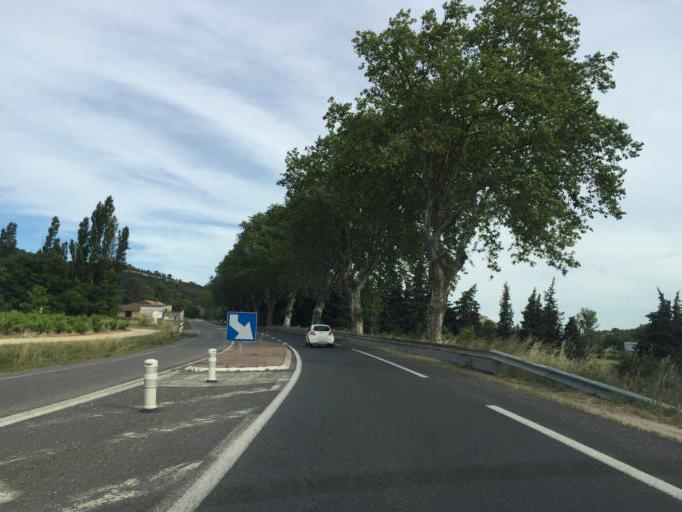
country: FR
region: Provence-Alpes-Cote d'Azur
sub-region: Departement du Vaucluse
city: Mondragon
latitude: 44.2234
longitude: 4.7156
